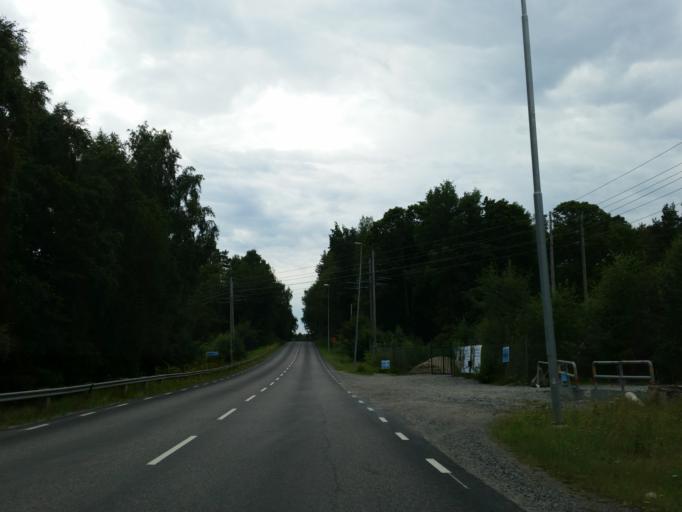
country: SE
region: Stockholm
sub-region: Botkyrka Kommun
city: Eriksberg
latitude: 59.2403
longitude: 17.7830
